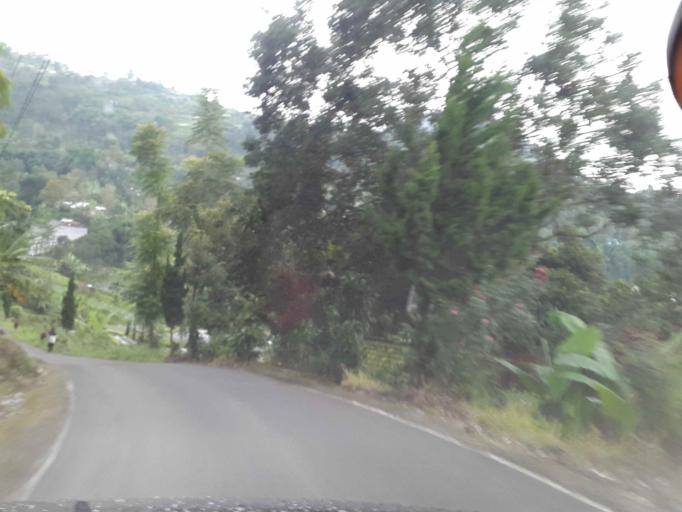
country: ID
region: Central Java
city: Sragen
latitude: -7.6280
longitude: 111.1186
